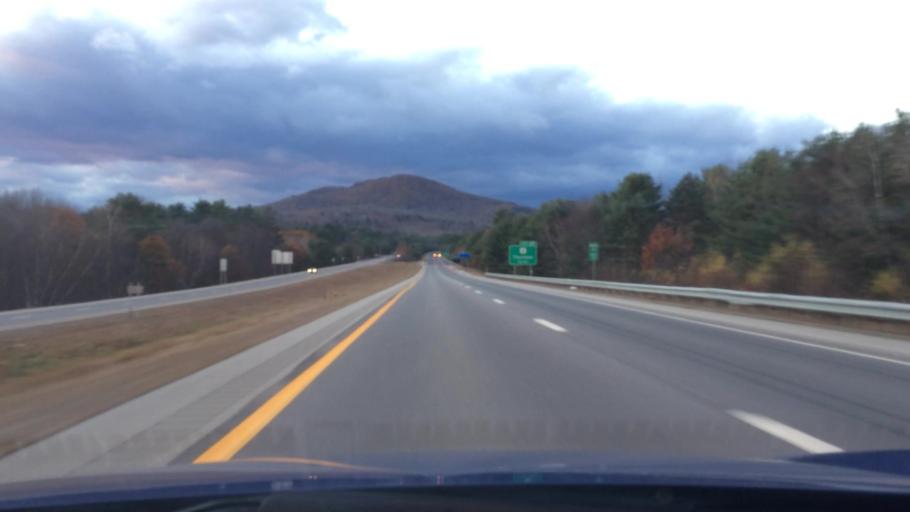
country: US
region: New Hampshire
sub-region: Grafton County
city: Thornton
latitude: 43.8644
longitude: -71.6588
